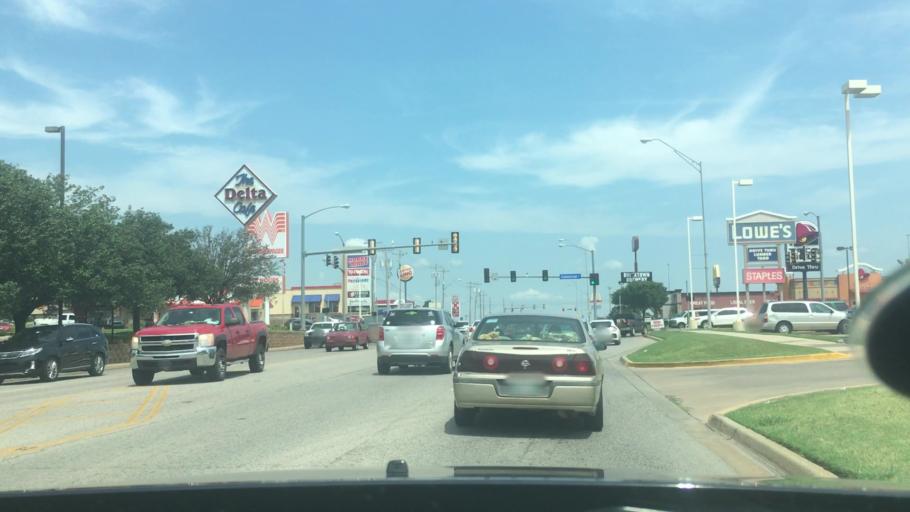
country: US
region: Oklahoma
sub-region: Pottawatomie County
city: Shawnee
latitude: 35.3800
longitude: -96.9297
